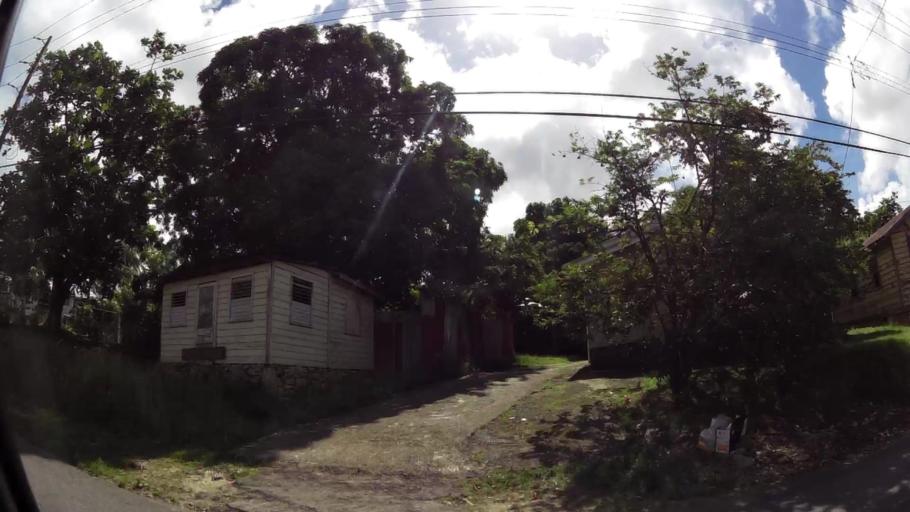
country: BB
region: Saint James
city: Holetown
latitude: 13.2037
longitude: -59.6087
